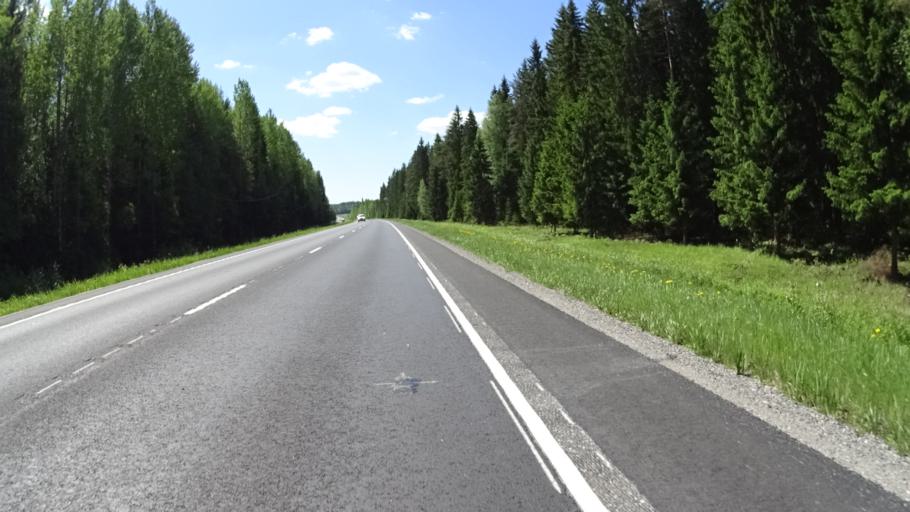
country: FI
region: Uusimaa
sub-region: Helsinki
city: Nurmijaervi
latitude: 60.4332
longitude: 24.8280
